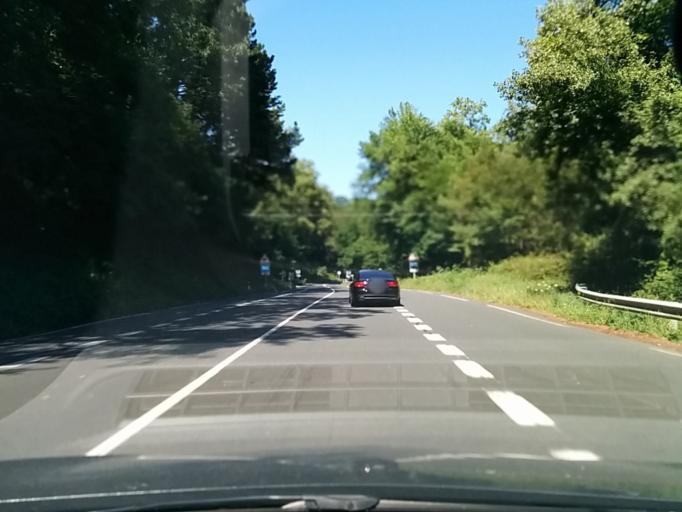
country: ES
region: Basque Country
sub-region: Provincia de Guipuzcoa
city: Deba
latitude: 43.2967
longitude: -2.3399
